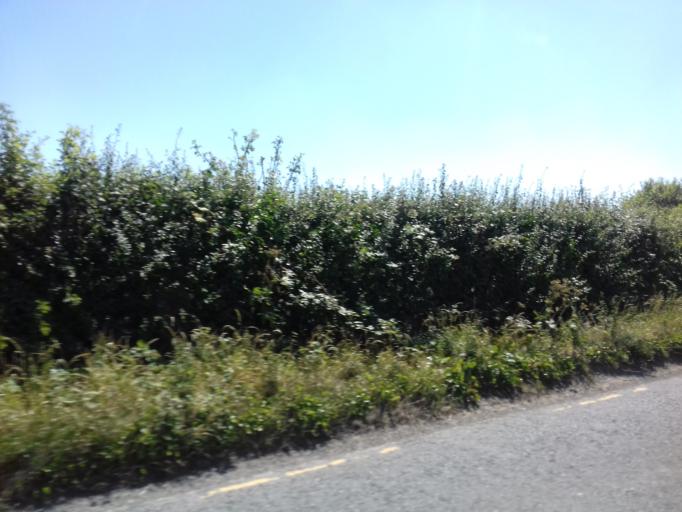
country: IE
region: Leinster
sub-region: Fingal County
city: Swords
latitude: 53.4909
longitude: -6.2690
